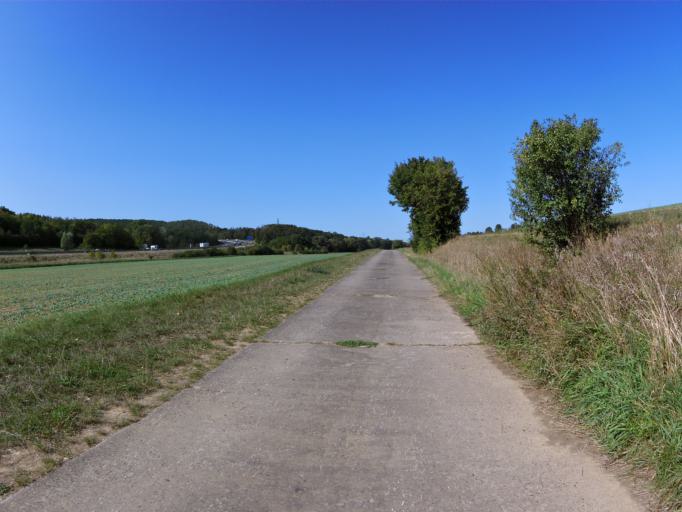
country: DE
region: Bavaria
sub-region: Regierungsbezirk Unterfranken
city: Waldbrunn
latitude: 49.7630
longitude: 9.7815
